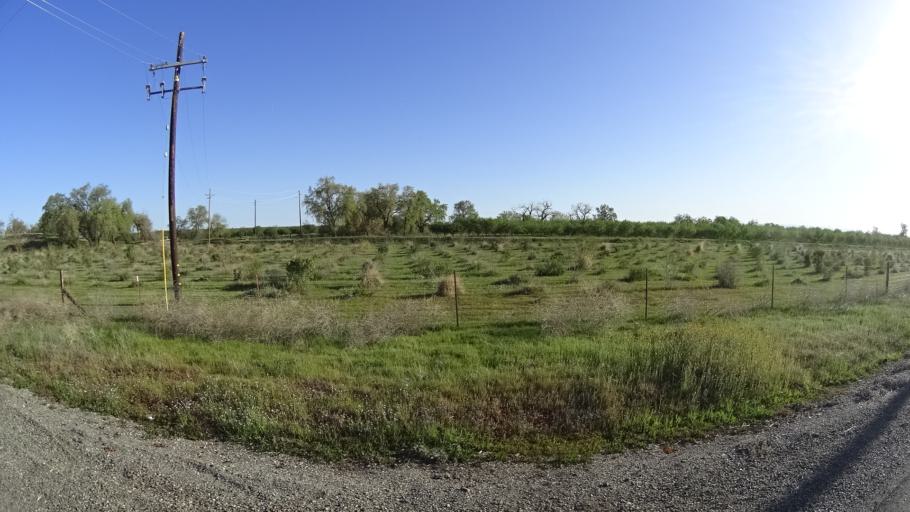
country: US
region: California
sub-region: Glenn County
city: Orland
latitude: 39.7809
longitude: -122.2923
